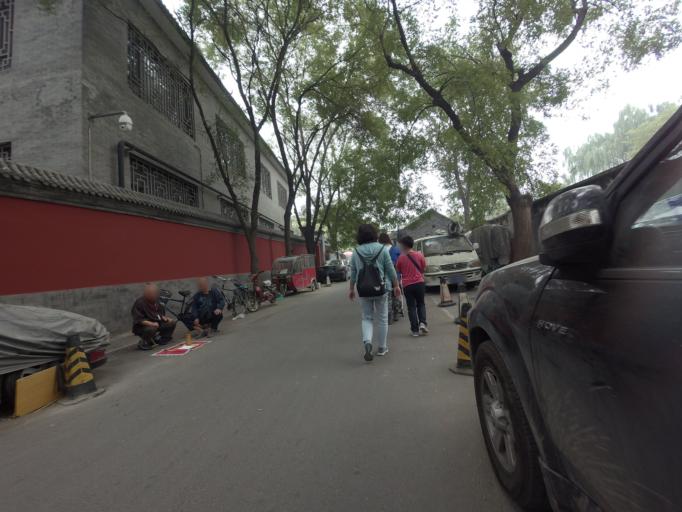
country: CN
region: Beijing
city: Jingshan
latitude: 39.9392
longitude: 116.3846
